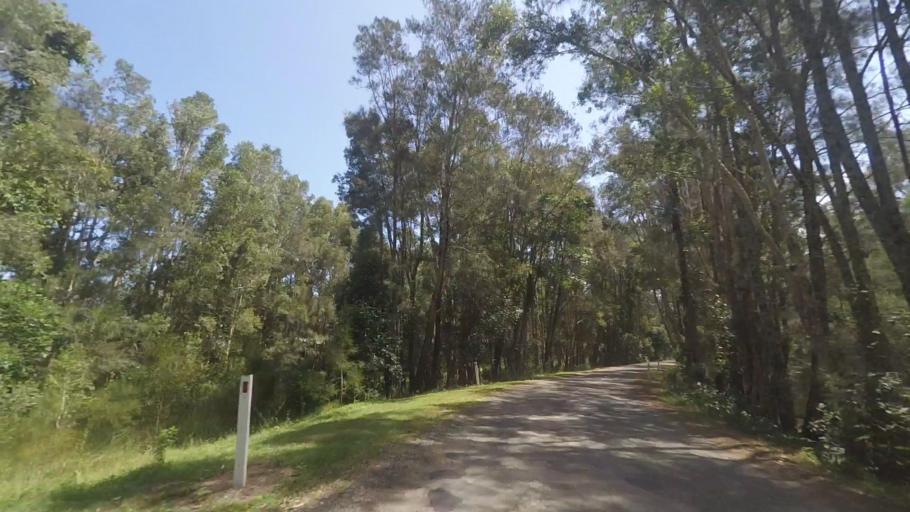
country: AU
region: New South Wales
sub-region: Great Lakes
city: Bulahdelah
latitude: -32.5079
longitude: 152.3019
